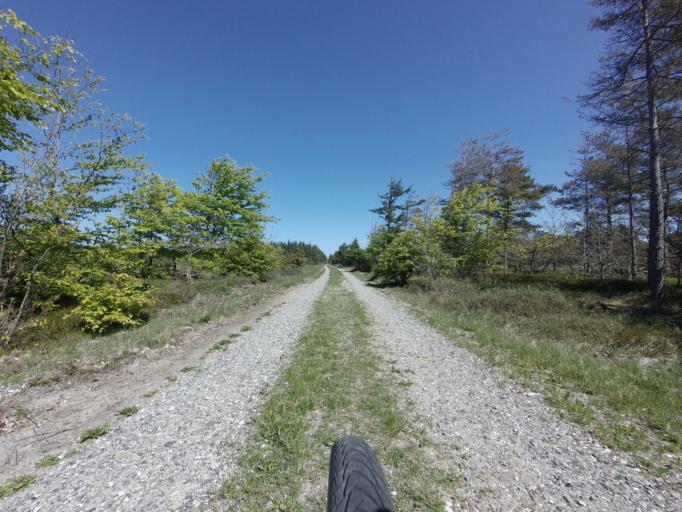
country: DK
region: North Denmark
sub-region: Jammerbugt Kommune
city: Kas
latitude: 57.2224
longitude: 9.5778
